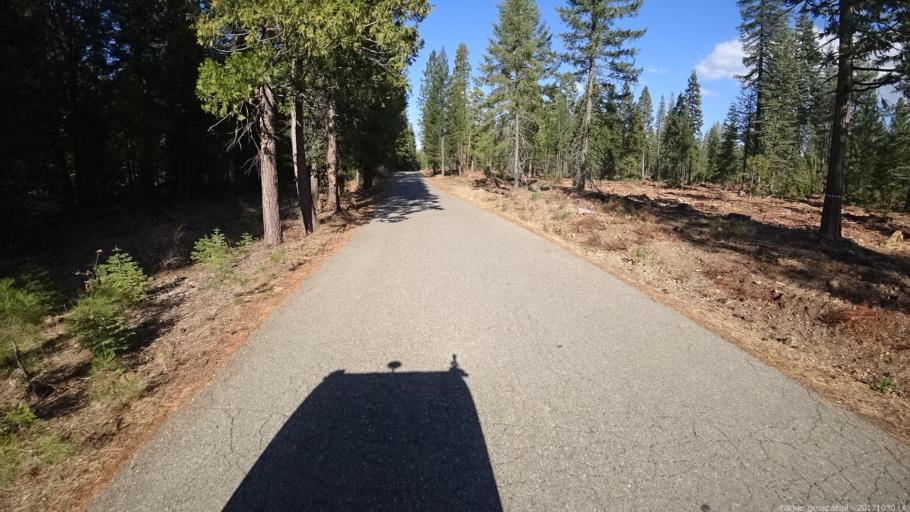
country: US
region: California
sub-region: Shasta County
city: Shingletown
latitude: 40.5140
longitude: -121.7255
